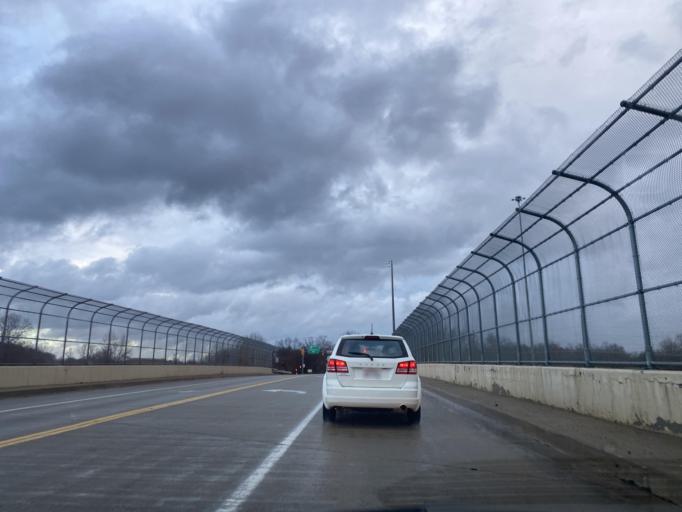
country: IN
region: Maharashtra
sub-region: Pune Division
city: Baramati
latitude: 18.1781
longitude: 74.4026
